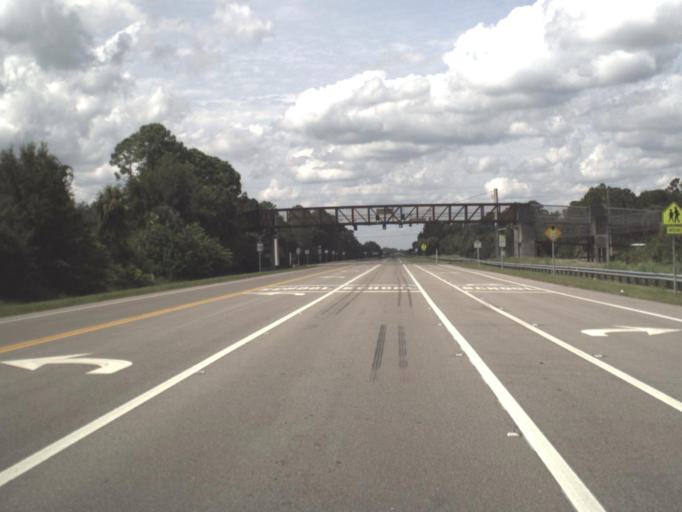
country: US
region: Florida
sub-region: Collier County
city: Immokalee
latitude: 26.4035
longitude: -81.3919
